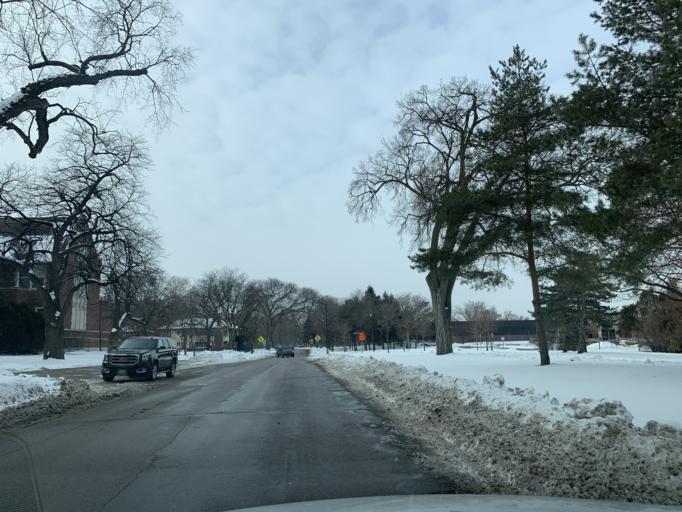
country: US
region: Minnesota
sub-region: Hennepin County
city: Minneapolis
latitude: 44.9699
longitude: -93.2931
